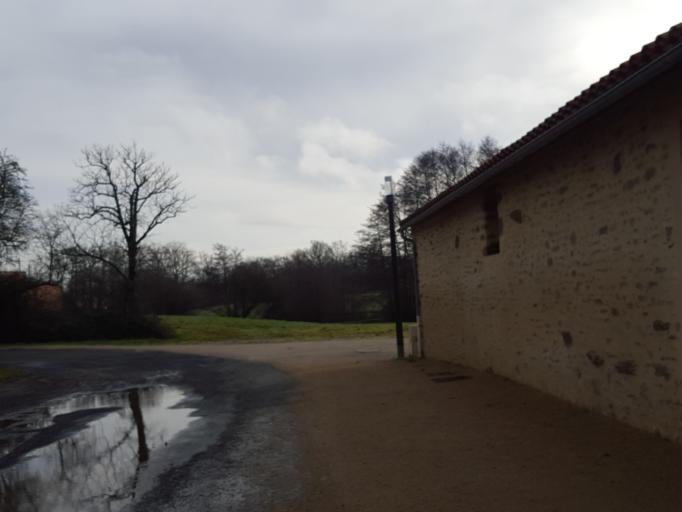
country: FR
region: Pays de la Loire
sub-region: Departement de la Vendee
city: Mouilleron-le-Captif
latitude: 46.7109
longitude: -1.4375
